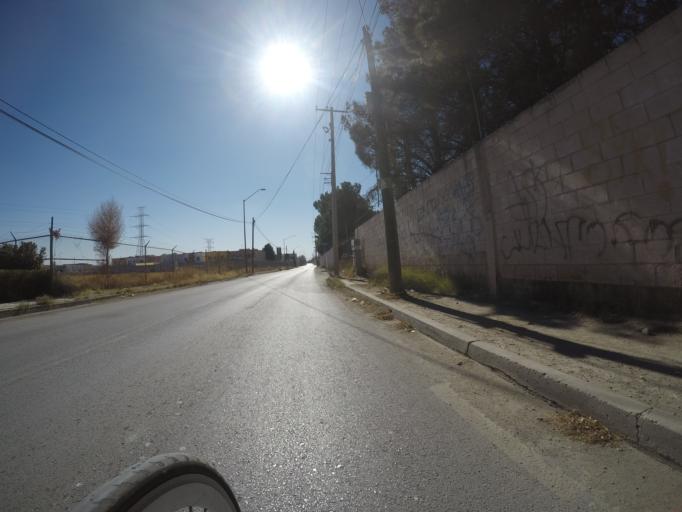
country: US
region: Texas
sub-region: El Paso County
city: Socorro
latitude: 31.6939
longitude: -106.3899
